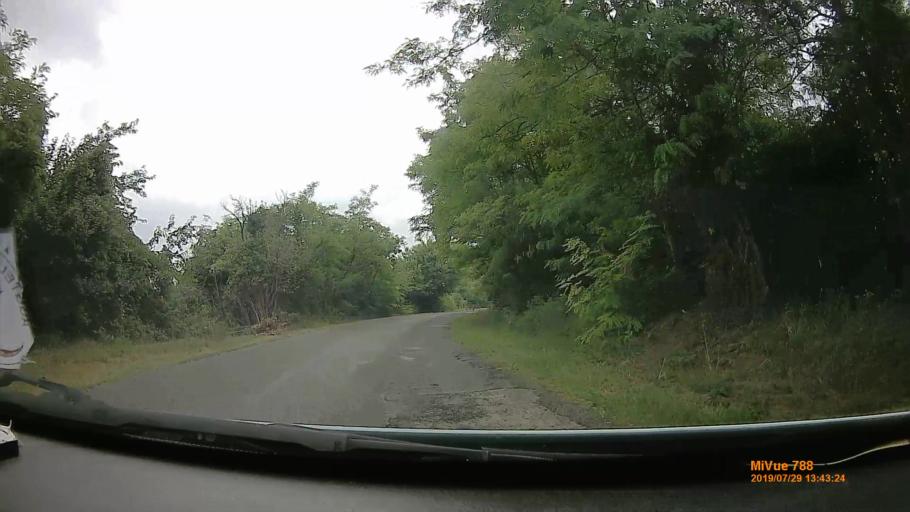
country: HU
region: Somogy
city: Balatonfoldvar
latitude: 46.8039
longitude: 17.9333
